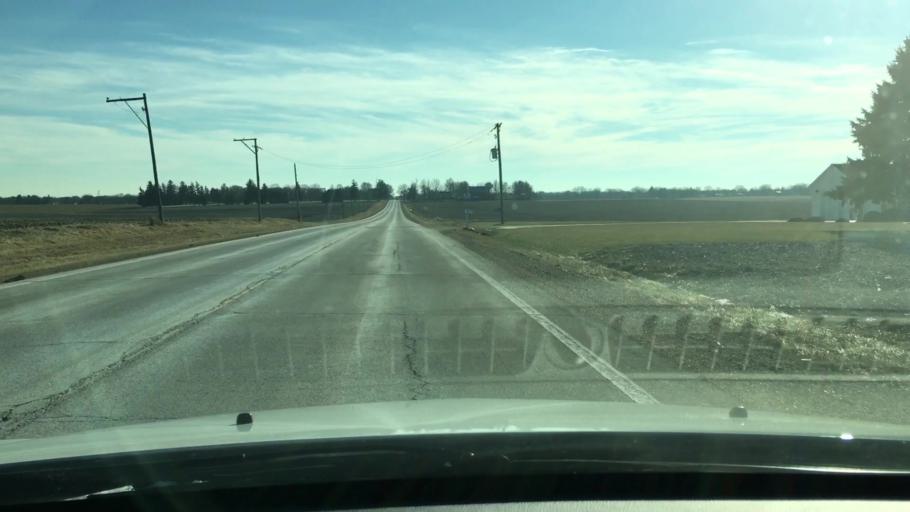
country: US
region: Illinois
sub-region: LaSalle County
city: Mendota
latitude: 41.5781
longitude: -89.1282
